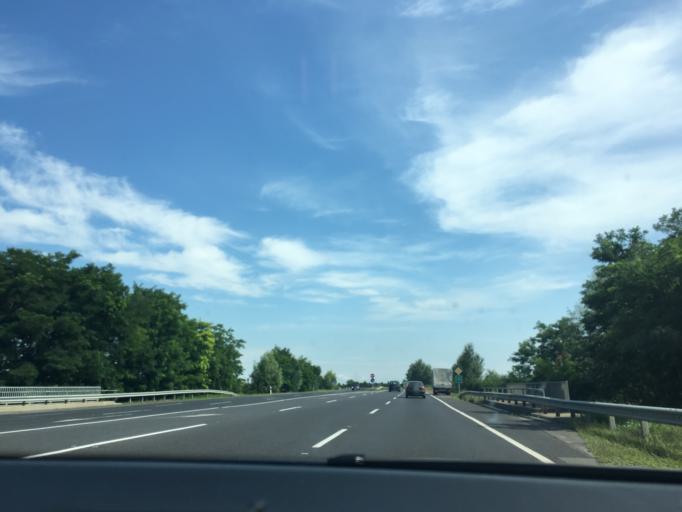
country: HU
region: Szabolcs-Szatmar-Bereg
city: Nyiregyhaza
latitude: 47.8846
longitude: 21.7097
